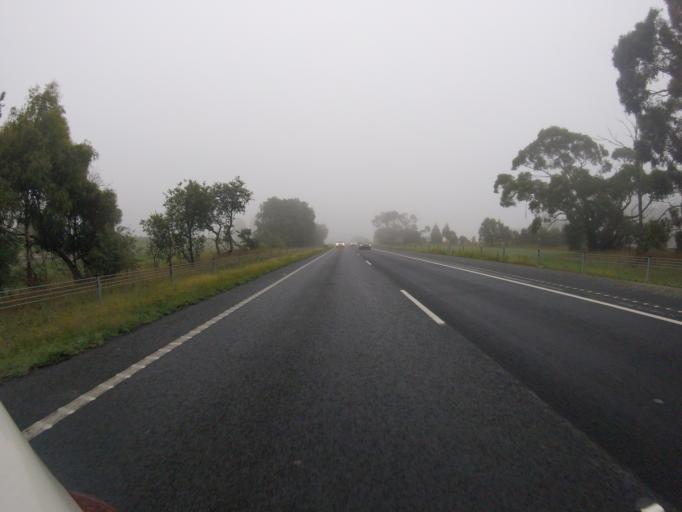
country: AU
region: Victoria
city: Brown Hill
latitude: -37.5507
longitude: 144.0168
